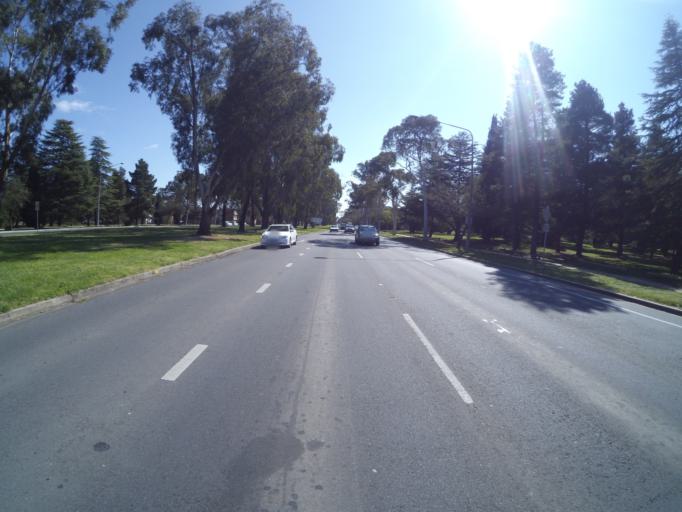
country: AU
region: Australian Capital Territory
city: Canberra
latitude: -35.2700
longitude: 149.1308
